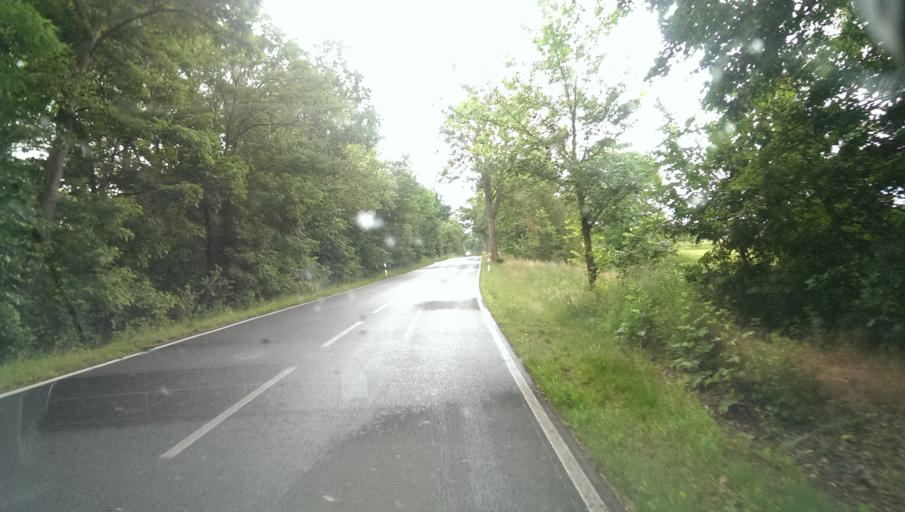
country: DE
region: Brandenburg
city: Stahnsdorf
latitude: 52.3509
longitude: 13.1940
